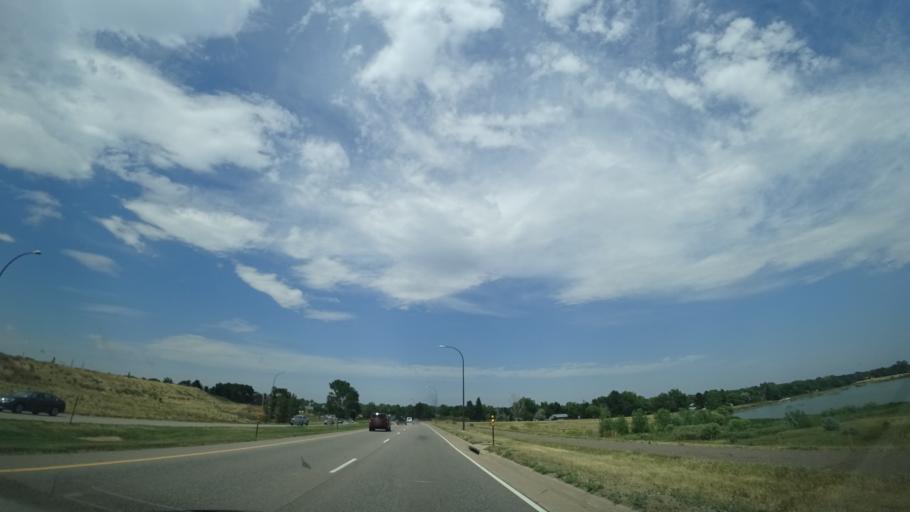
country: US
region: Colorado
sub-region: Jefferson County
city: Lakewood
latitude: 39.6924
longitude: -105.1145
